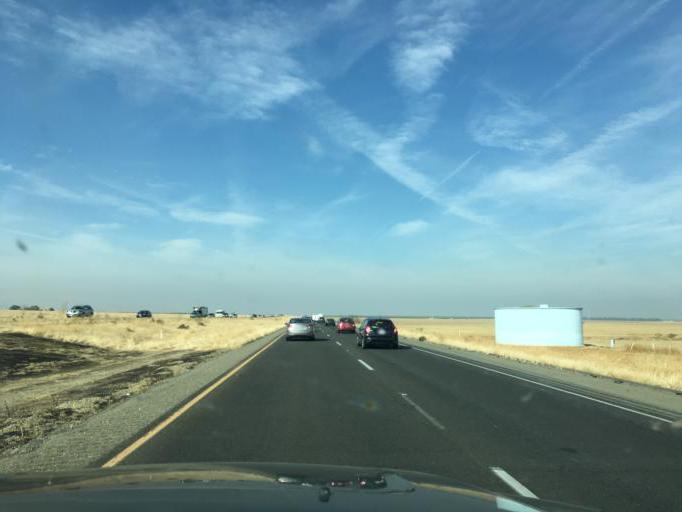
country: US
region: California
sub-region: Fresno County
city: Coalinga
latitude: 36.3405
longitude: -120.3088
